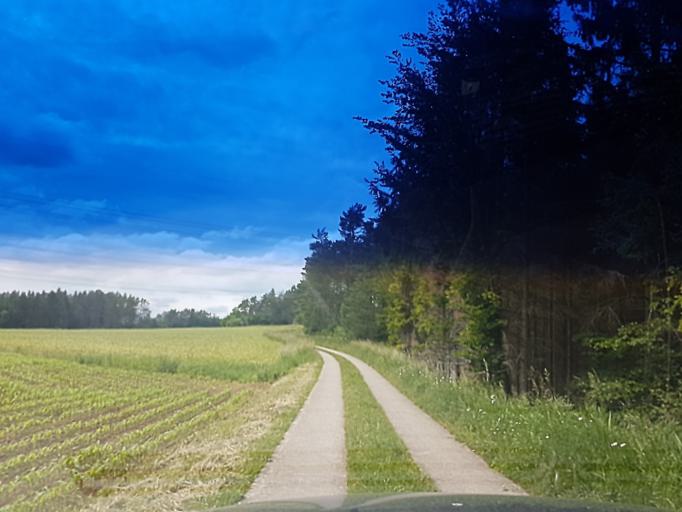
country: DE
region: Bavaria
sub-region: Upper Franconia
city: Wattendorf
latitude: 50.0093
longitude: 11.1233
